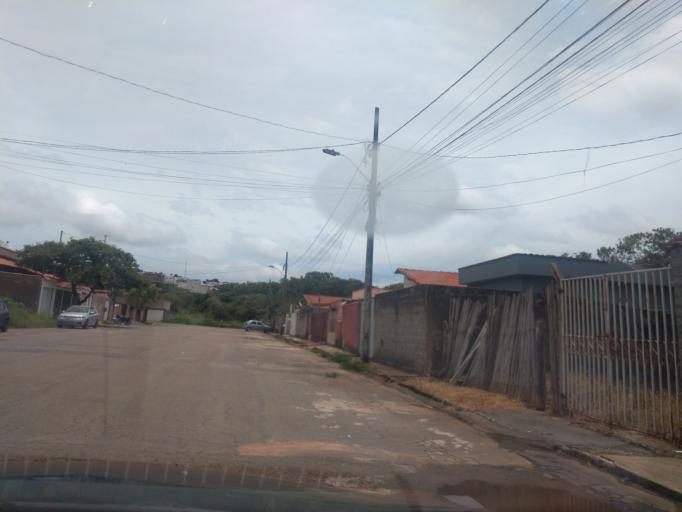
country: BR
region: Minas Gerais
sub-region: Tres Coracoes
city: Tres Coracoes
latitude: -21.6797
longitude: -45.2602
